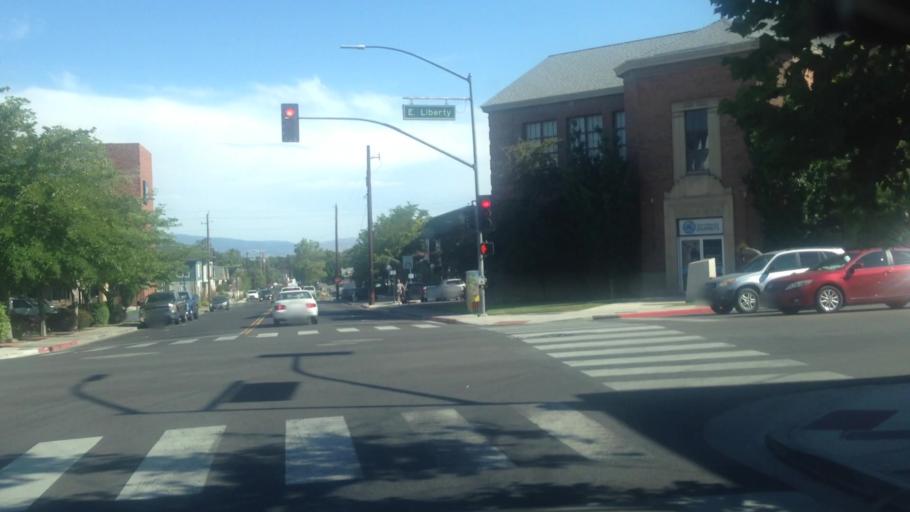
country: US
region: Nevada
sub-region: Washoe County
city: Reno
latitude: 39.5229
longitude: -119.8088
